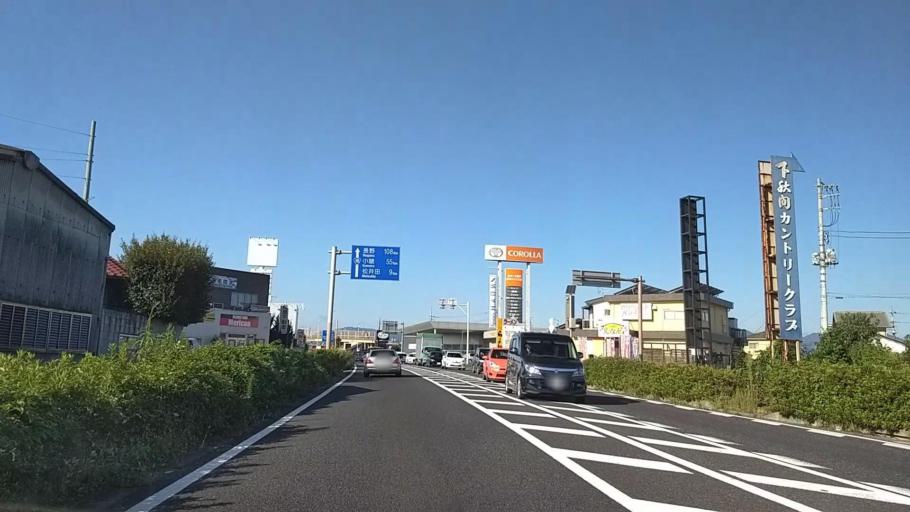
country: JP
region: Gunma
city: Annaka
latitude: 36.3275
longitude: 138.8863
